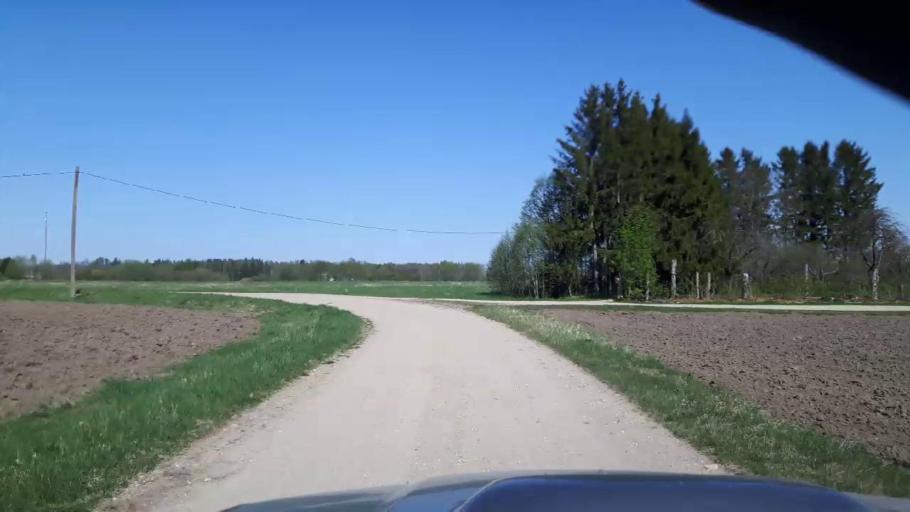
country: EE
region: Paernumaa
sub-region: Sindi linn
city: Sindi
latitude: 58.4451
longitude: 24.7813
